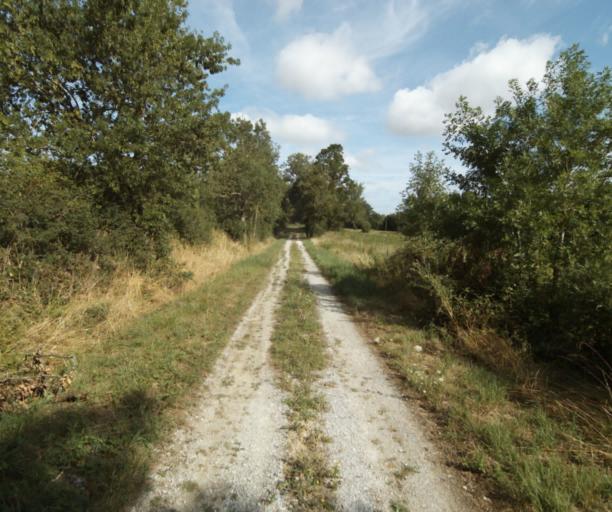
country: FR
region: Midi-Pyrenees
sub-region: Departement du Tarn
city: Soreze
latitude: 43.4722
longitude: 2.0810
